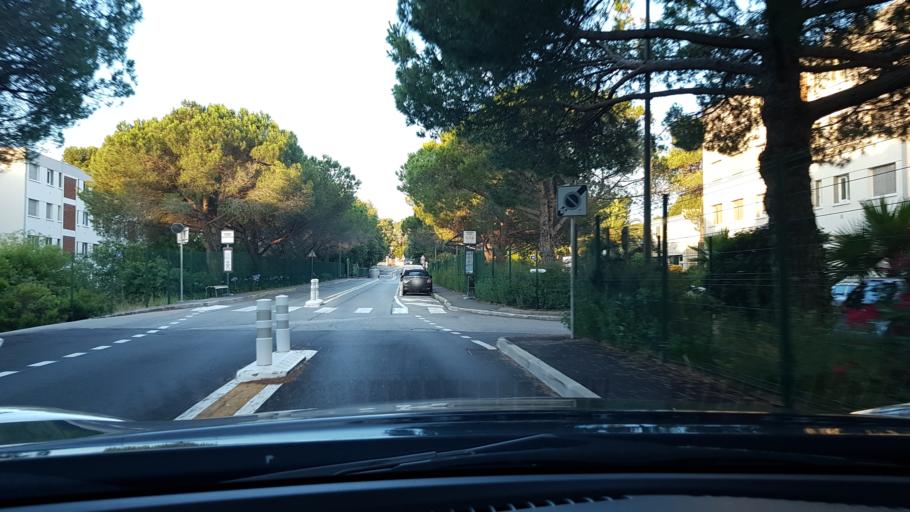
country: FR
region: Provence-Alpes-Cote d'Azur
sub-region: Departement des Alpes-Maritimes
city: Vallauris
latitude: 43.5862
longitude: 7.0447
